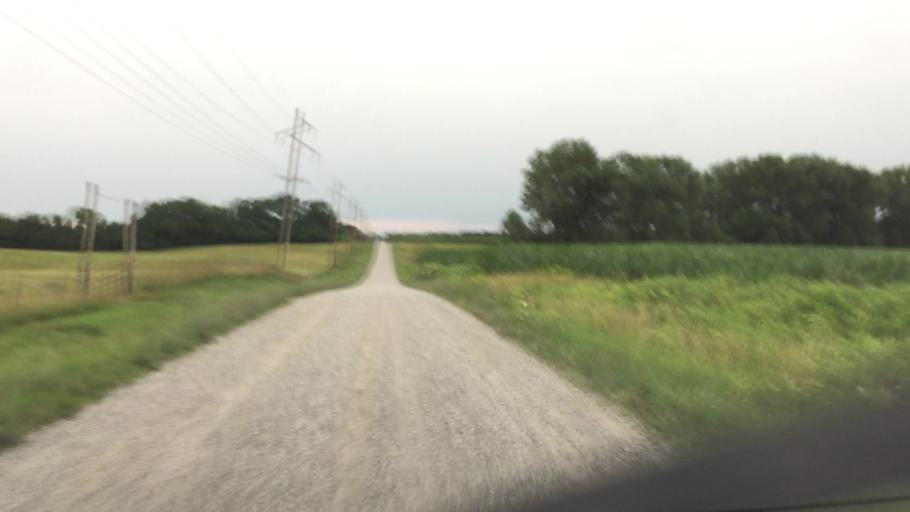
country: US
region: Illinois
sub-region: Hancock County
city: Hamilton
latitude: 40.4261
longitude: -91.3430
